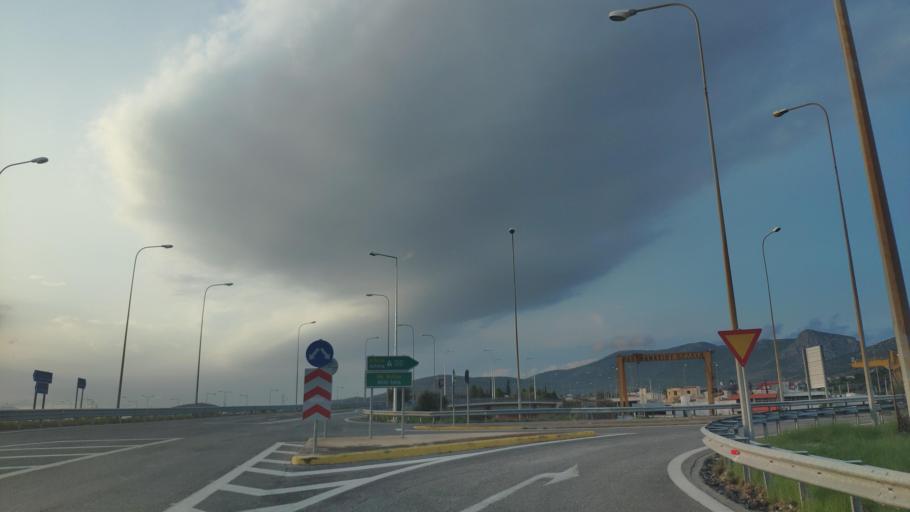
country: GR
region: Attica
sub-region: Nomarchia Dytikis Attikis
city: Vlychada
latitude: 38.0194
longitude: 23.4308
